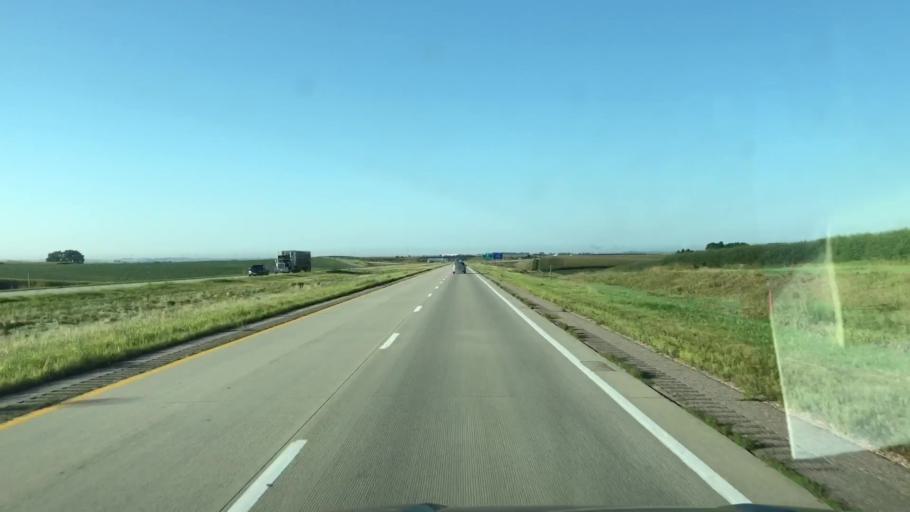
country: US
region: Iowa
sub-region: Plymouth County
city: Le Mars
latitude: 42.8031
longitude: -96.2005
